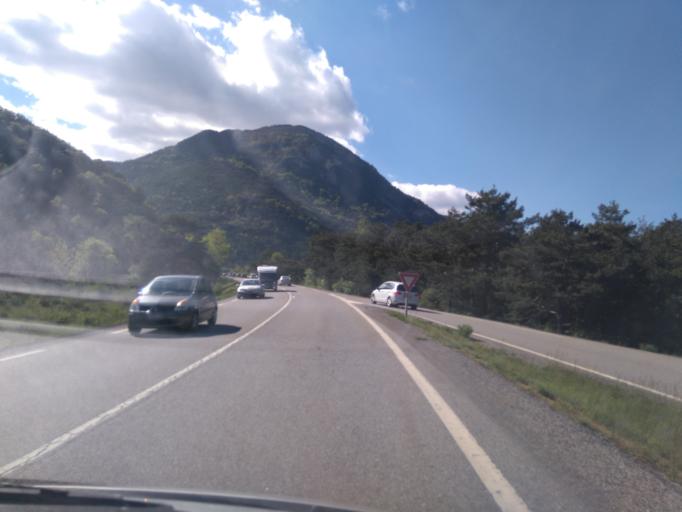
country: FR
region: Provence-Alpes-Cote d'Azur
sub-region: Departement des Hautes-Alpes
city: Veynes
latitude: 44.5933
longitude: 5.7164
